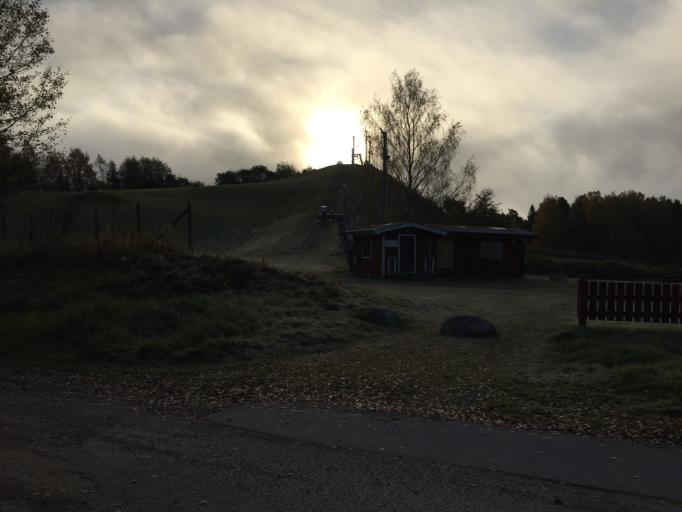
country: SE
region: Vaestmanland
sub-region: Hallstahammars Kommun
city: Hallstahammar
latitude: 59.6282
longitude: 16.2467
